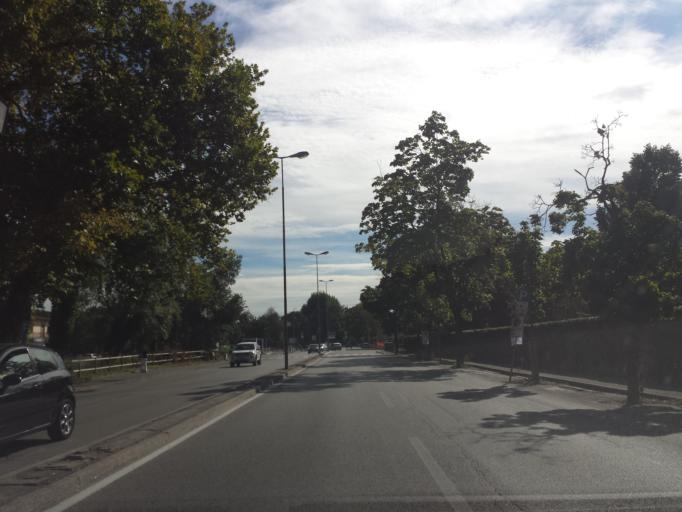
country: IT
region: Veneto
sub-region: Provincia di Vicenza
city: Vicenza
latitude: 45.5578
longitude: 11.5472
